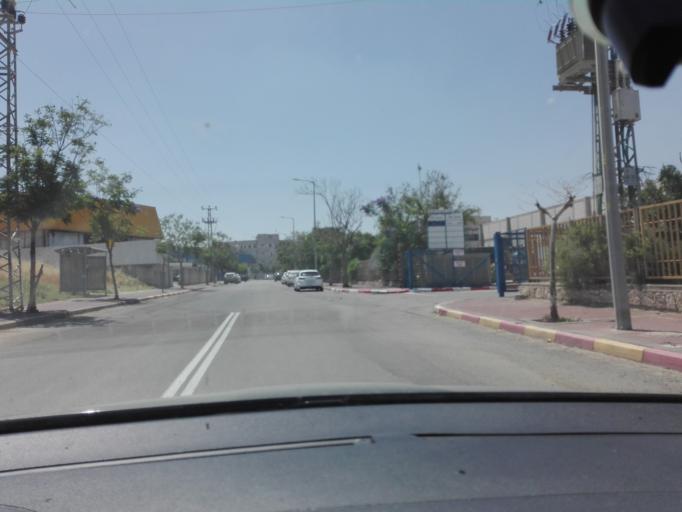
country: IL
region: Southern District
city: Qiryat Gat
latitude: 31.5936
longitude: 34.7799
